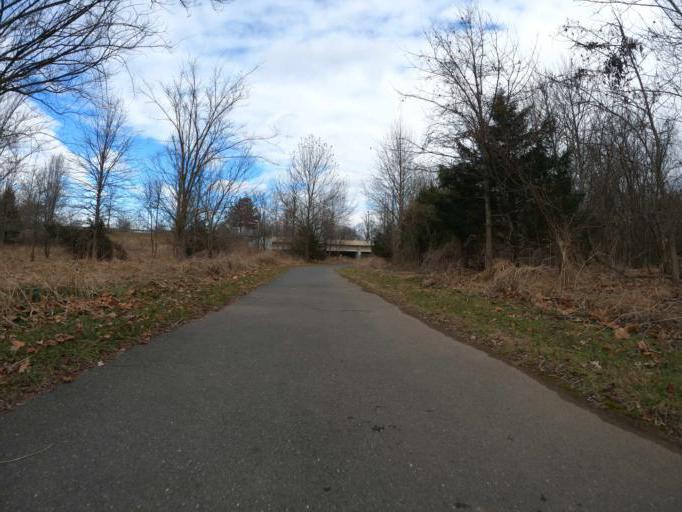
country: US
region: Maryland
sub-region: Frederick County
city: Ballenger Creek
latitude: 39.3703
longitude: -77.4156
